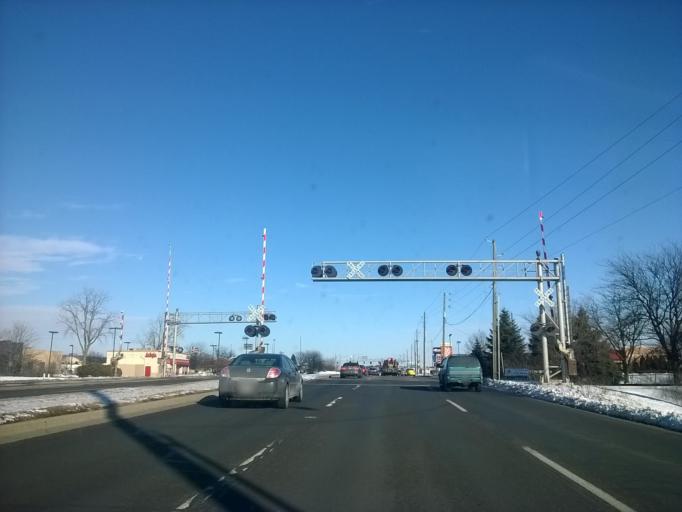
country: US
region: Indiana
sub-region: Hamilton County
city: Fishers
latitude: 39.9270
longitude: -86.0371
